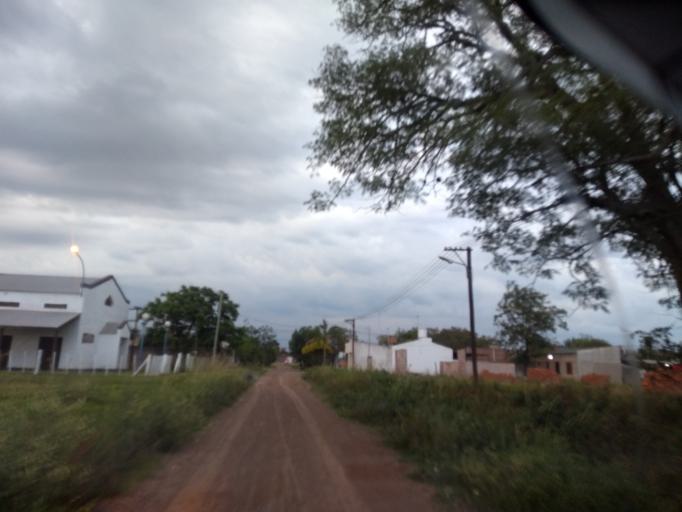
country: AR
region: Chaco
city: Fontana
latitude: -27.4108
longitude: -59.0330
